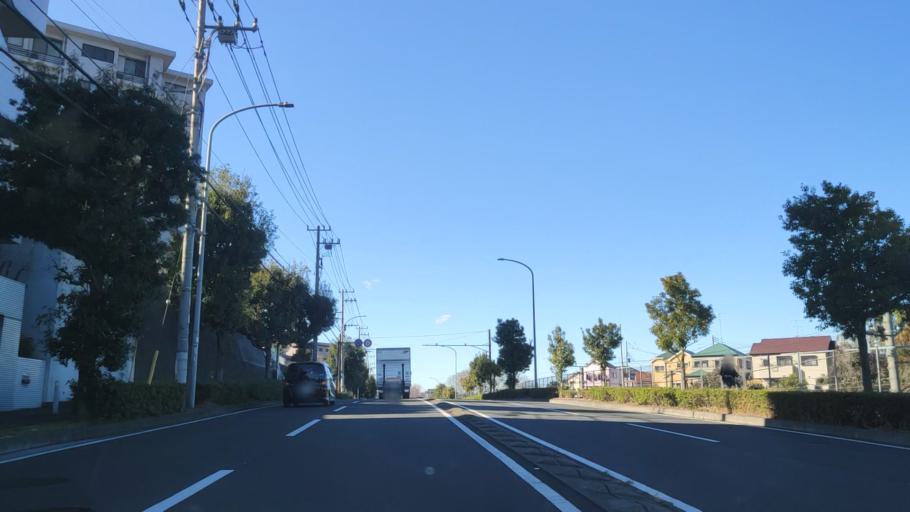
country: JP
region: Tokyo
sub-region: Machida-shi
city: Machida
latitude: 35.5207
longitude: 139.5274
